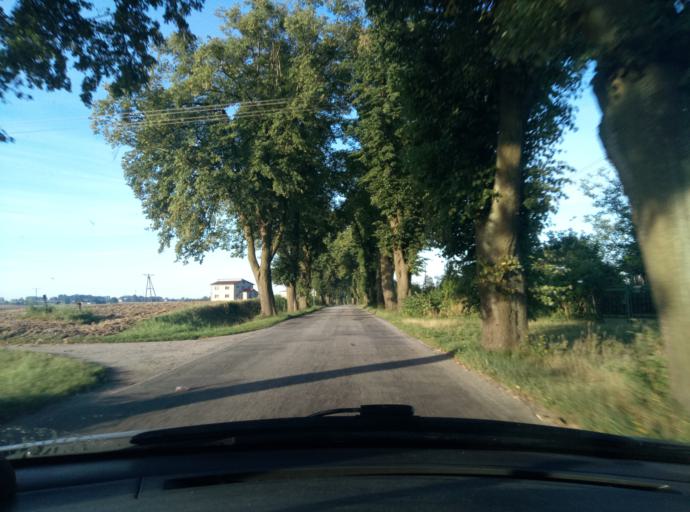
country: PL
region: Kujawsko-Pomorskie
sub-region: Powiat brodnicki
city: Jablonowo Pomorskie
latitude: 53.4059
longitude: 19.1717
